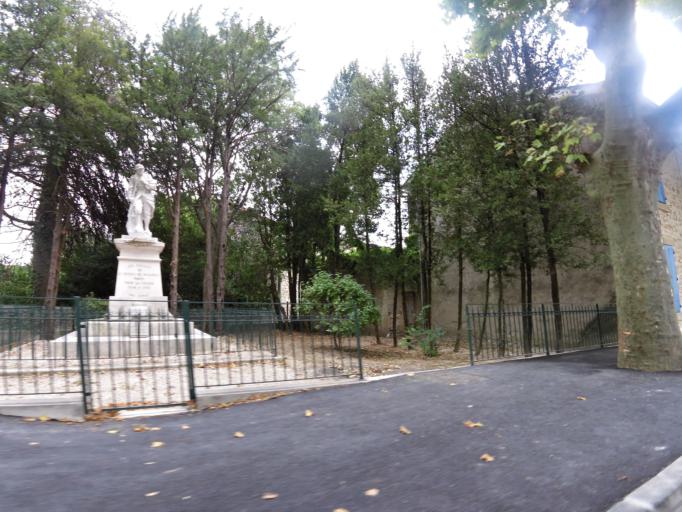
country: FR
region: Languedoc-Roussillon
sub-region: Departement du Gard
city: Saint-Genies-de-Malgoires
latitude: 43.9475
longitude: 4.2156
